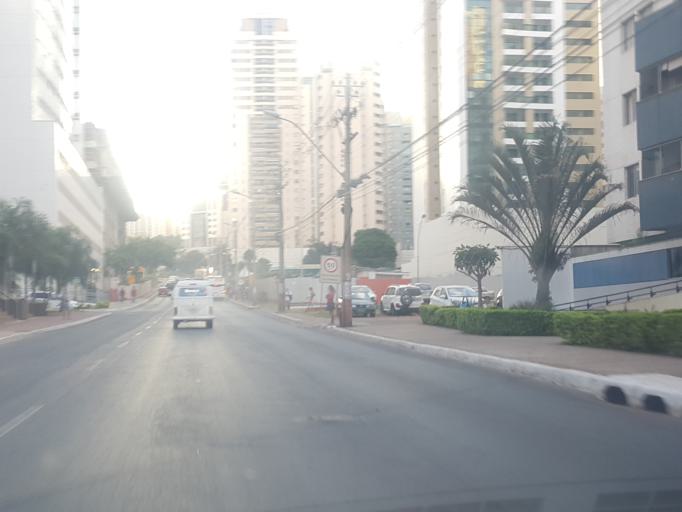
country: BR
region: Federal District
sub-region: Brasilia
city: Brasilia
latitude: -15.8385
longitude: -48.0279
